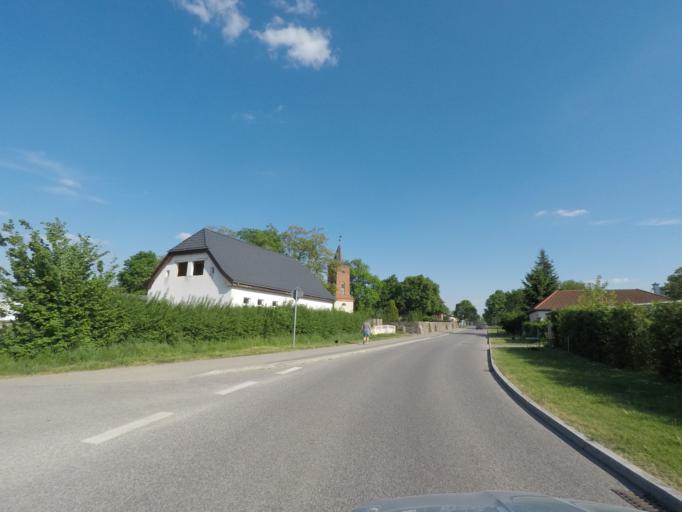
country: DE
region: Brandenburg
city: Hohenfinow
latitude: 52.7304
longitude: 13.8700
